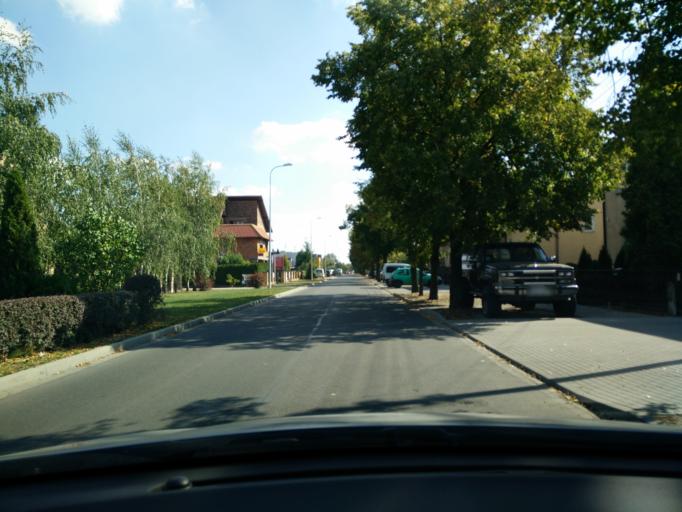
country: PL
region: Greater Poland Voivodeship
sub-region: Powiat sredzki
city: Sroda Wielkopolska
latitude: 52.2363
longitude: 17.2545
